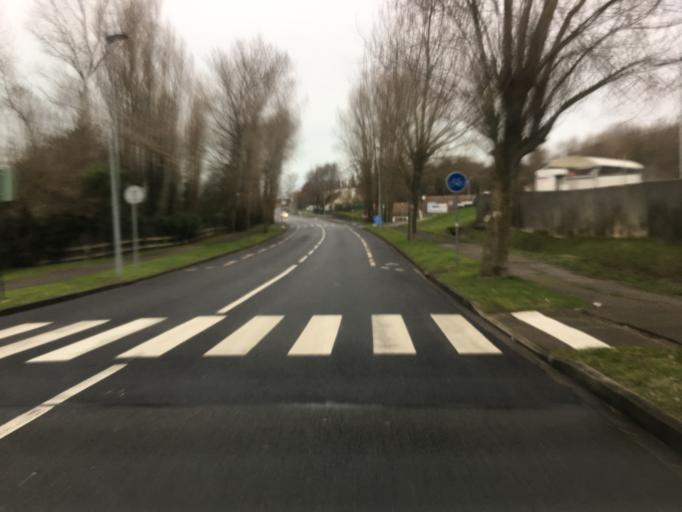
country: FR
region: Nord-Pas-de-Calais
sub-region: Departement du Pas-de-Calais
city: Le Portel
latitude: 50.6986
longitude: 1.5802
